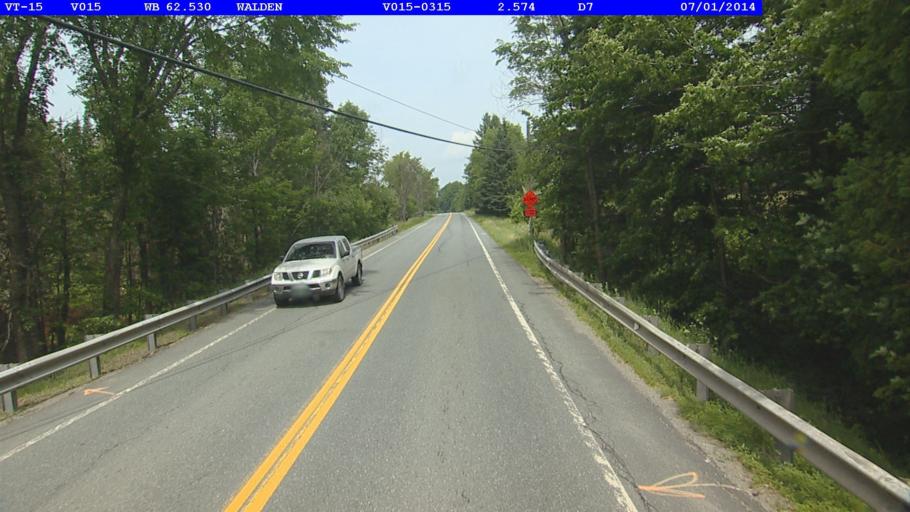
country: US
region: Vermont
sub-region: Caledonia County
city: Hardwick
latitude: 44.4627
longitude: -72.2656
